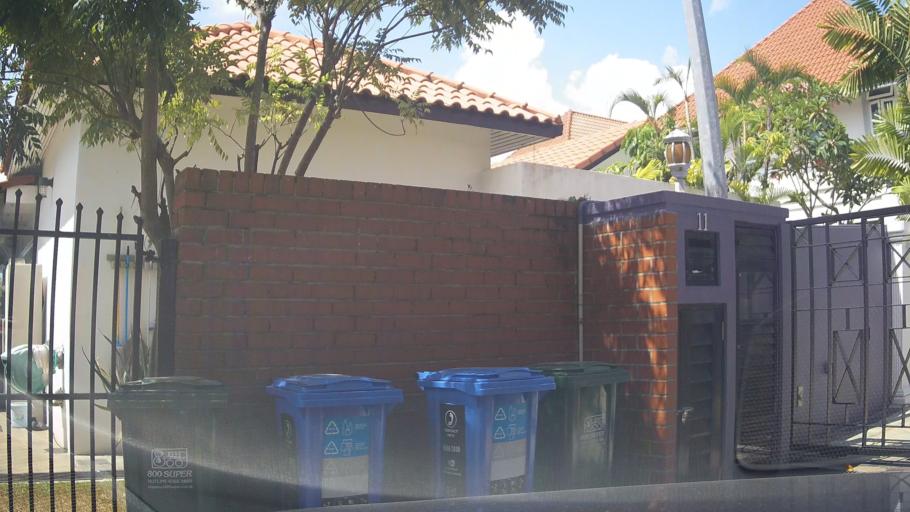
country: MY
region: Johor
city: Kampung Pasir Gudang Baru
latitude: 1.3655
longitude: 103.9745
